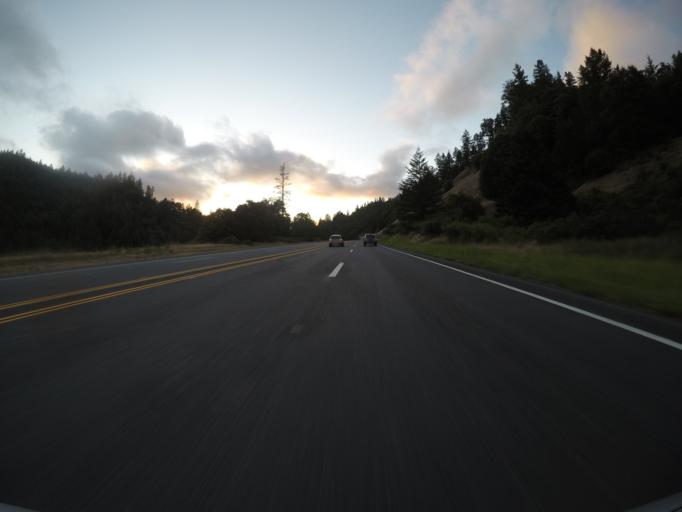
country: US
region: California
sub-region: Humboldt County
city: Redway
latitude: 40.0419
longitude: -123.7798
